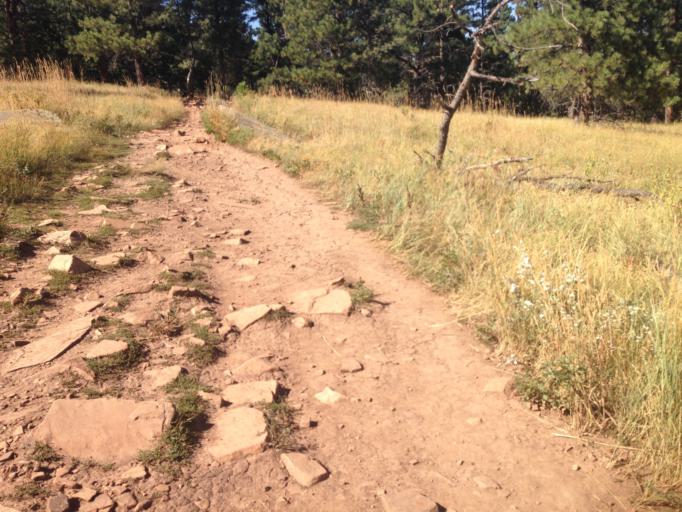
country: US
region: Colorado
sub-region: Boulder County
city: Boulder
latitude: 39.9824
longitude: -105.2853
